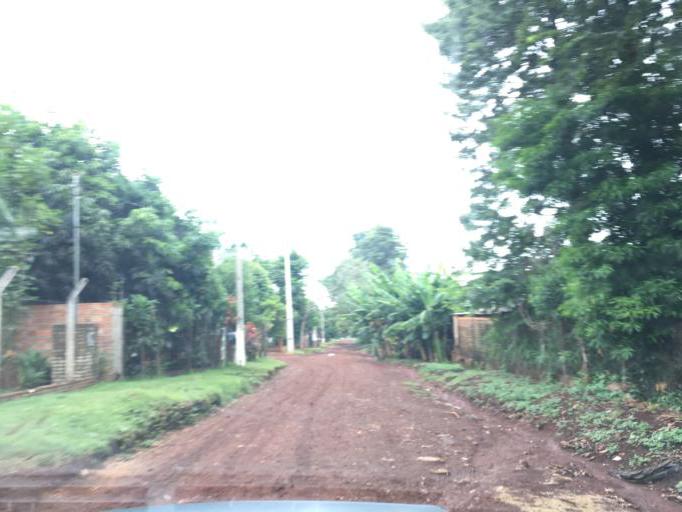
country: PY
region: Alto Parana
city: Ciudad del Este
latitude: -25.4218
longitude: -54.6412
